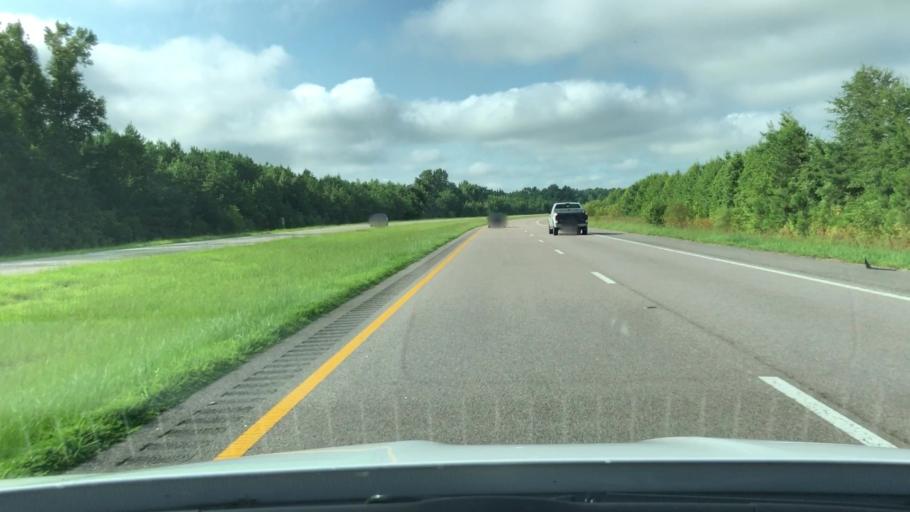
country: US
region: Virginia
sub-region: City of Portsmouth
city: Portsmouth Heights
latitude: 36.6559
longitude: -76.3544
